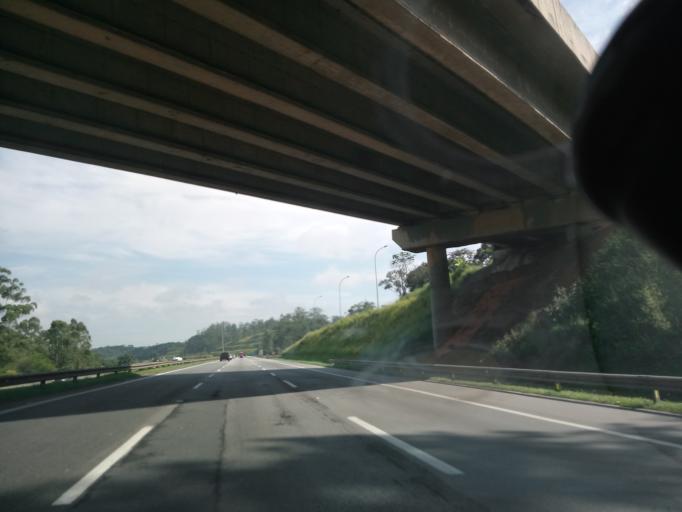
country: BR
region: Sao Paulo
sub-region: Itapecerica Da Serra
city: Itapecerica da Serra
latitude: -23.6918
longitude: -46.8187
